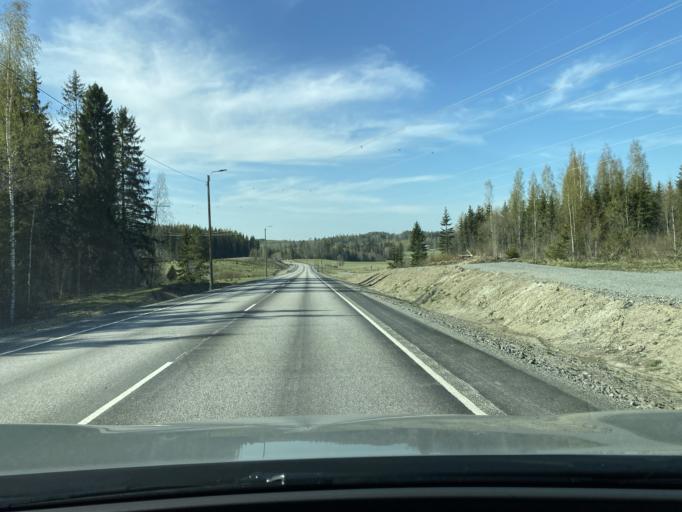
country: FI
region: Uusimaa
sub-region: Helsinki
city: Nurmijaervi
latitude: 60.4110
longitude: 24.7498
